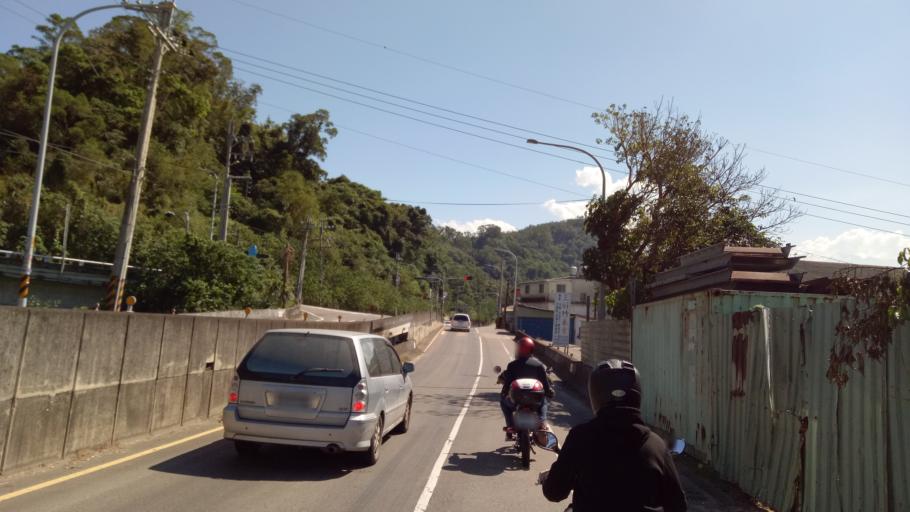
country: TW
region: Taiwan
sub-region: Hsinchu
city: Hsinchu
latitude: 24.6828
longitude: 120.9633
